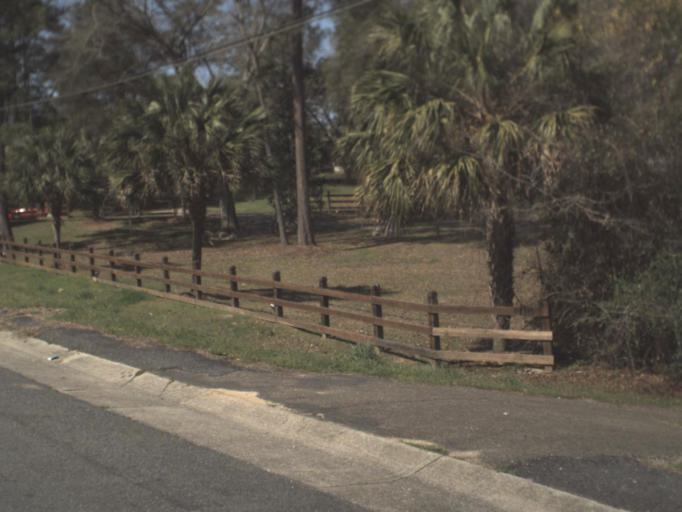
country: US
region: Florida
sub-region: Gadsden County
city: Quincy
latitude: 30.5933
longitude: -84.5484
